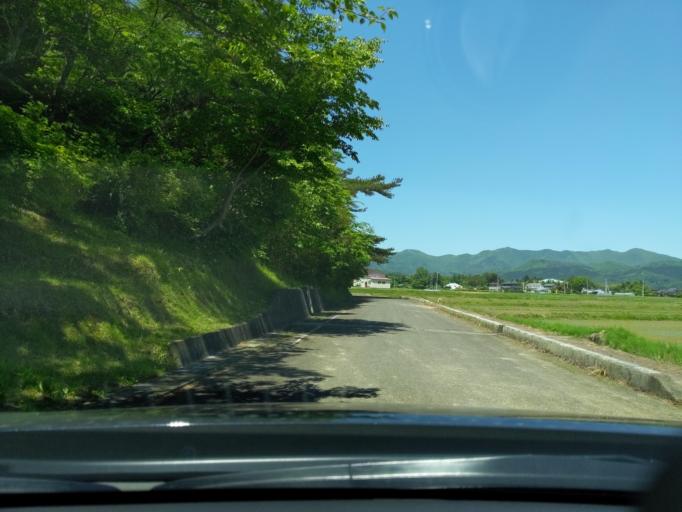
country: JP
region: Fukushima
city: Koriyama
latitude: 37.3897
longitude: 140.2754
